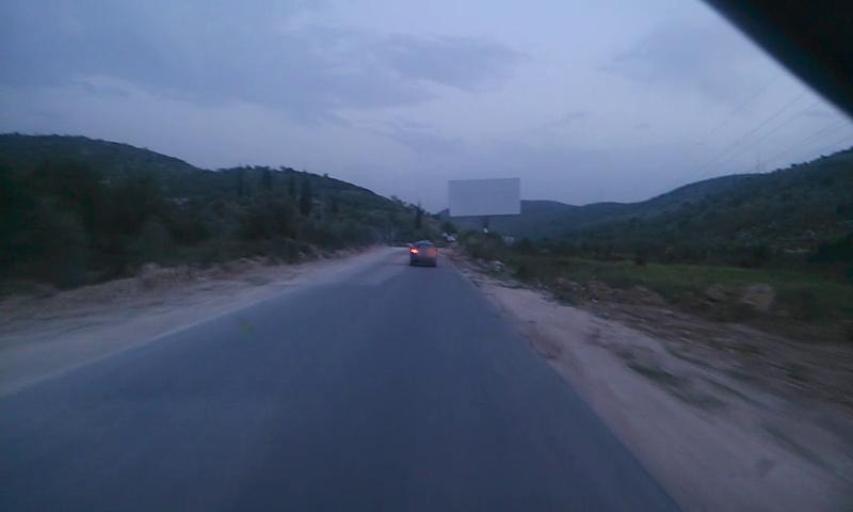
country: PS
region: West Bank
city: `Anabta
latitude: 32.2964
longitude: 35.1323
